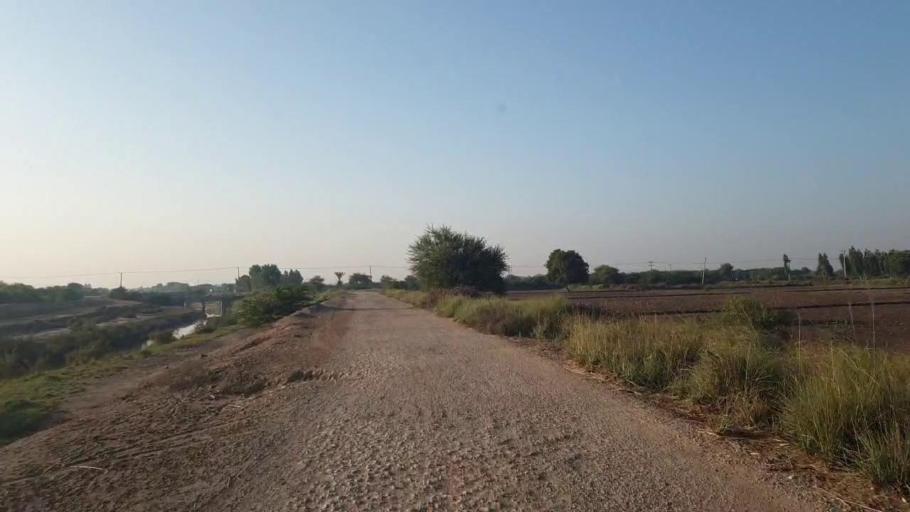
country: PK
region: Sindh
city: Badin
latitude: 24.6519
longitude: 68.7894
